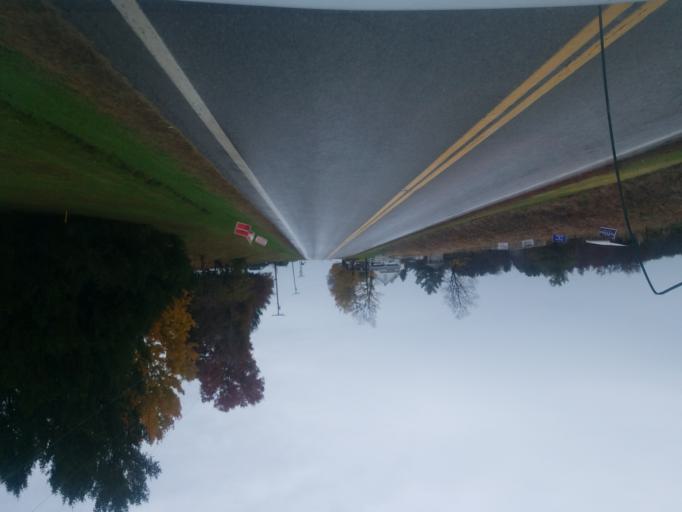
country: US
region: Ohio
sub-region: Morgan County
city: McConnelsville
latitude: 39.4808
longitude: -81.8698
